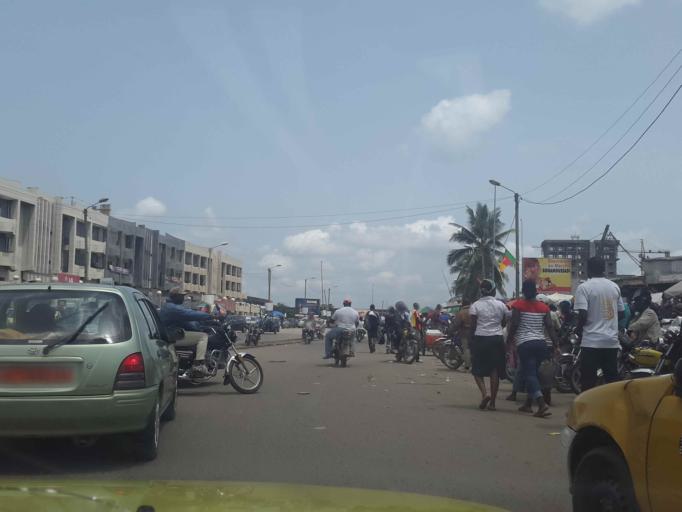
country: CM
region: Littoral
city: Douala
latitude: 4.0926
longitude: 9.7391
